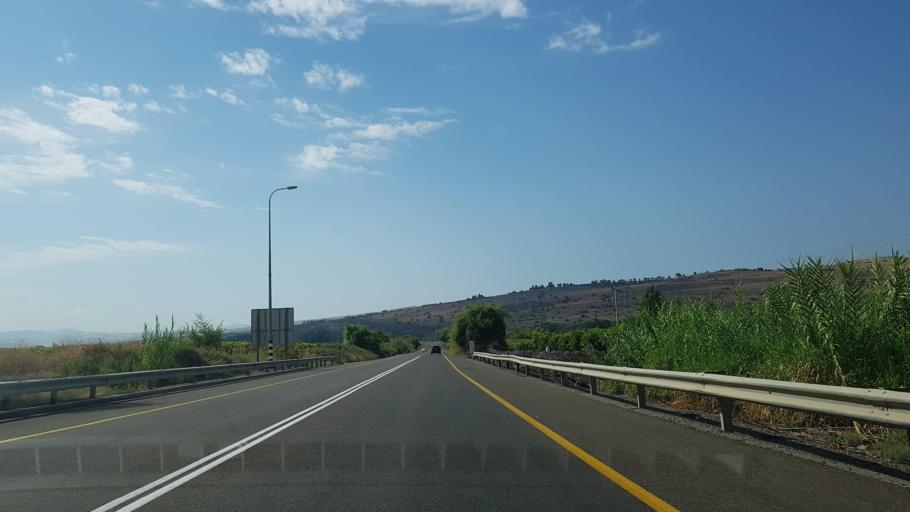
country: SY
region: Quneitra
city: Al Butayhah
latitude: 32.9043
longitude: 35.6325
